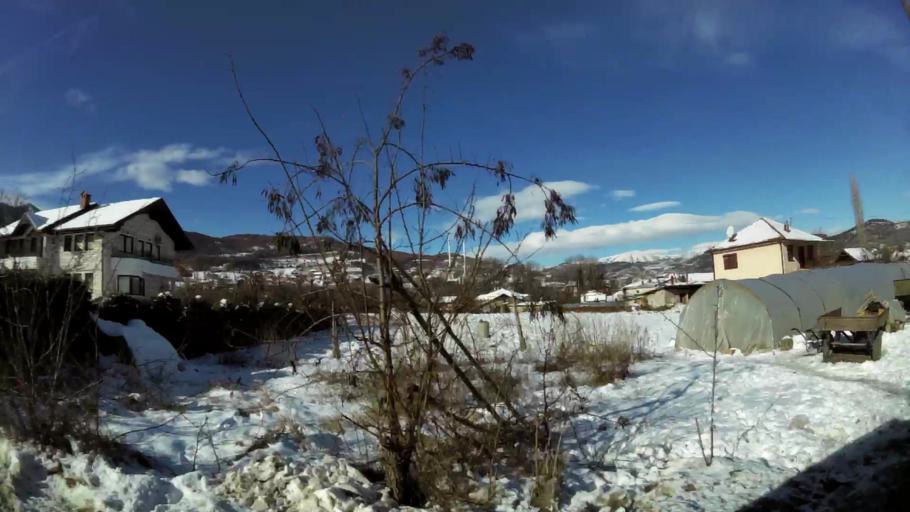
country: MK
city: Grchec
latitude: 41.9782
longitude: 21.3093
